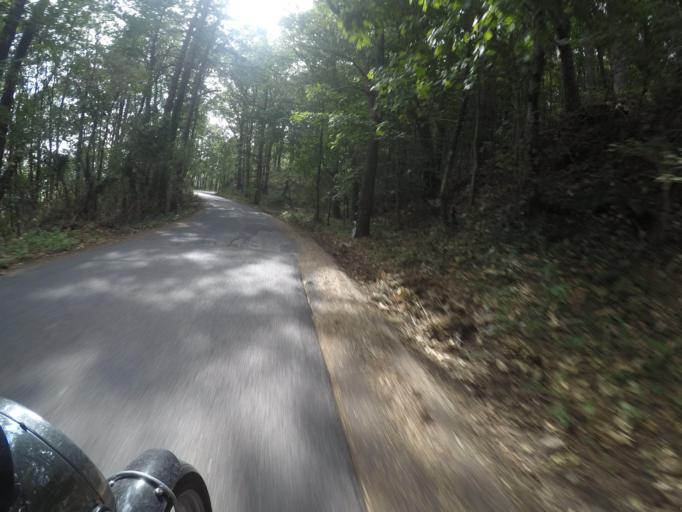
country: IT
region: Tuscany
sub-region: Provincia di Massa-Carrara
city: Fosdinovo
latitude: 44.1209
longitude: 10.0728
